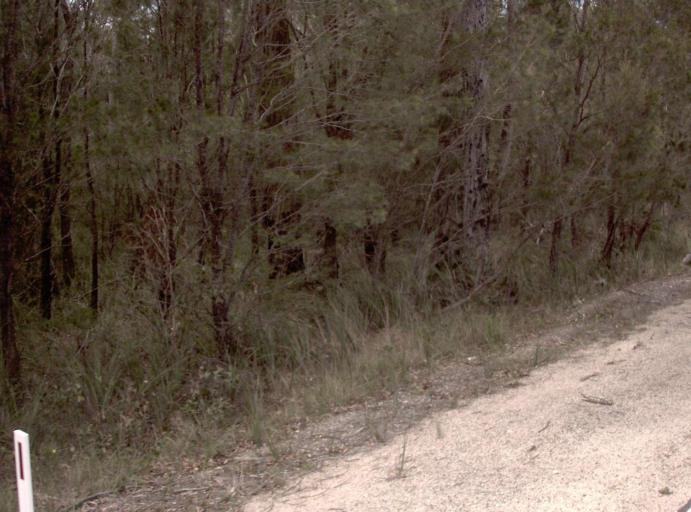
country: AU
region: New South Wales
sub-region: Bega Valley
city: Eden
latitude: -37.4487
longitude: 149.6237
